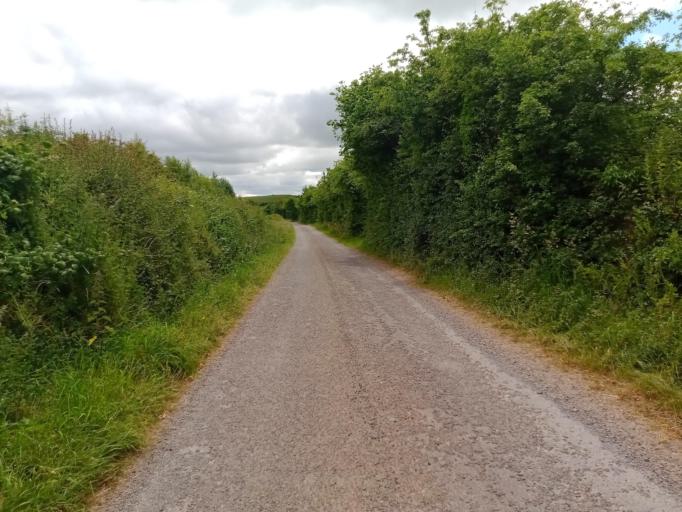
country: IE
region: Leinster
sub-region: Laois
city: Rathdowney
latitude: 52.7911
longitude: -7.4811
